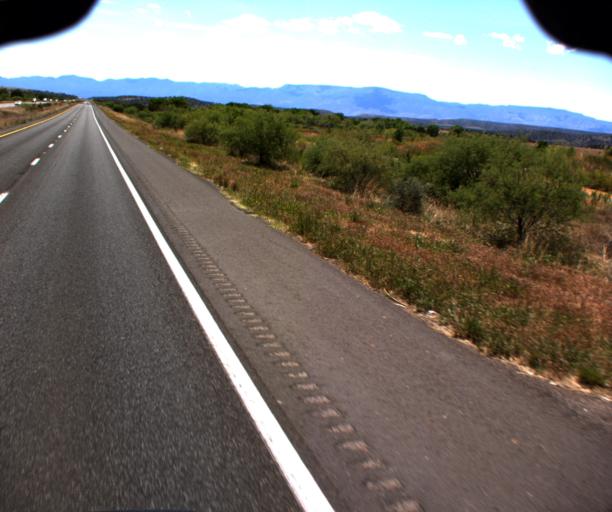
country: US
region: Arizona
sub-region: Yavapai County
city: West Sedona
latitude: 34.8290
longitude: -111.8945
